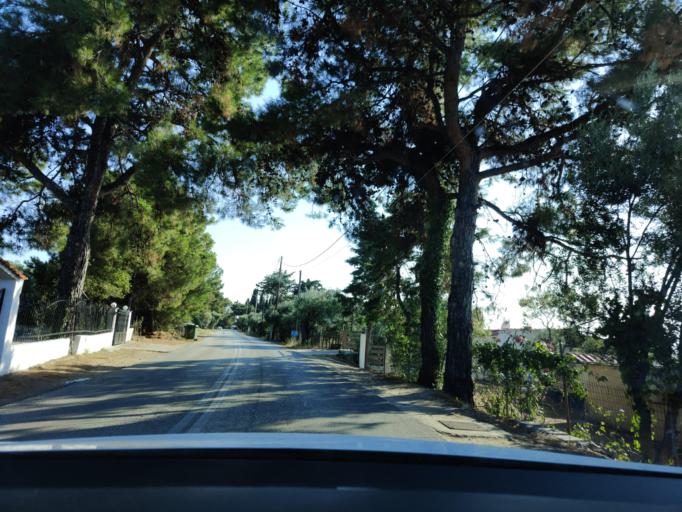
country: GR
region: East Macedonia and Thrace
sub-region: Nomos Kavalas
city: Prinos
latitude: 40.6982
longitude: 24.5268
